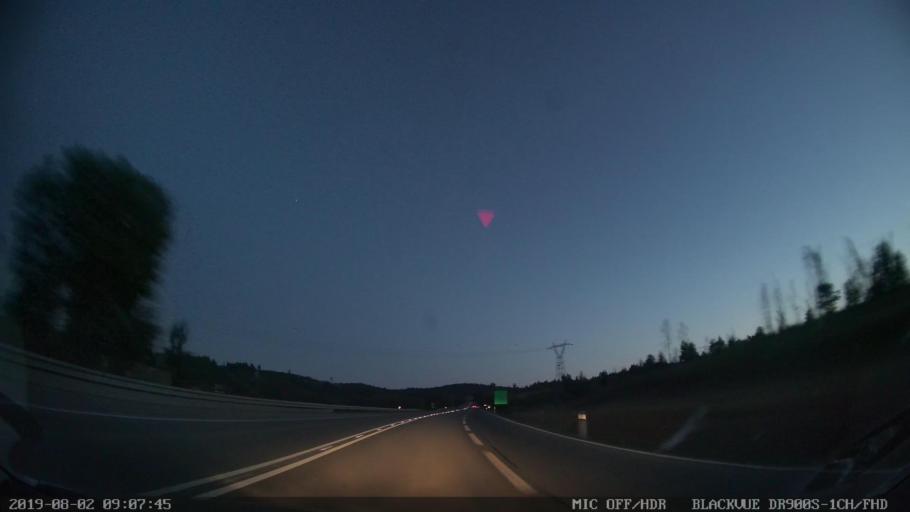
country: PT
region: Portalegre
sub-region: Nisa
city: Nisa
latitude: 39.5134
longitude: -7.7687
